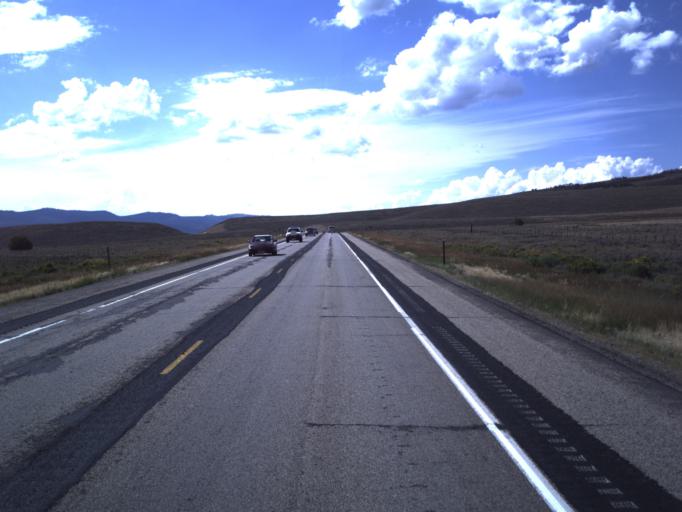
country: US
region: Utah
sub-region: Wasatch County
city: Heber
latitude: 40.2267
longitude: -111.1127
